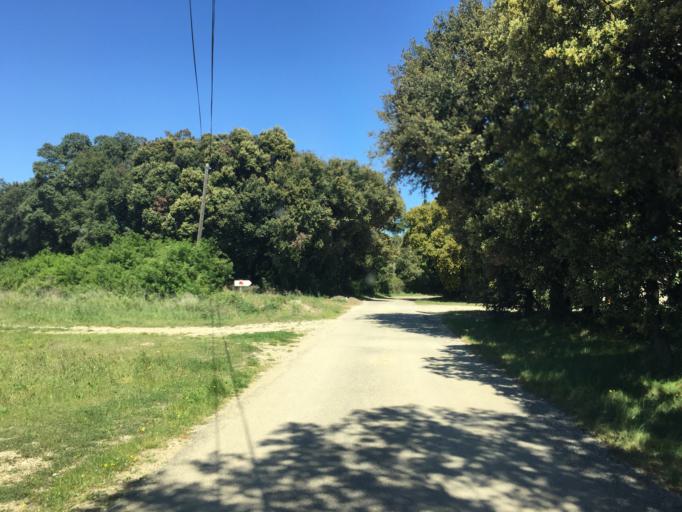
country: FR
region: Provence-Alpes-Cote d'Azur
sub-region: Departement du Vaucluse
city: Jonquieres
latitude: 44.1409
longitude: 4.9169
